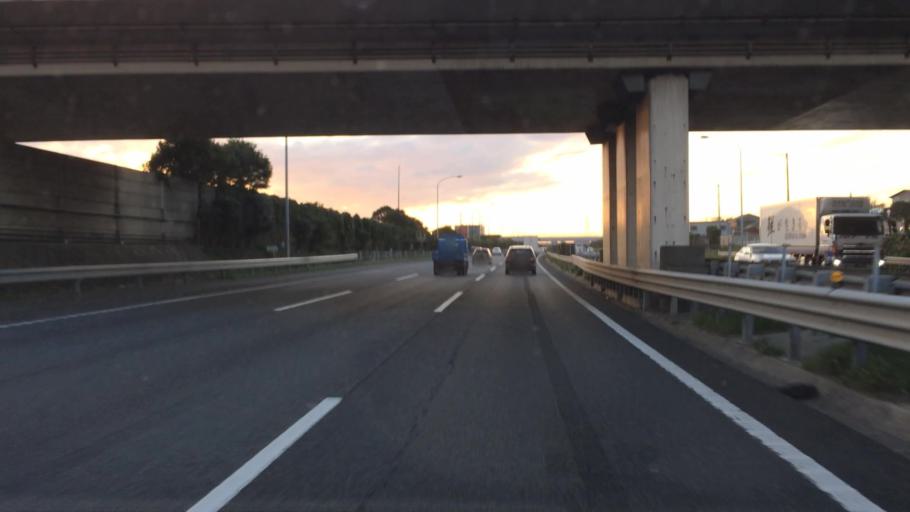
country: JP
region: Chiba
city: Yotsukaido
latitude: 35.6823
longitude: 140.1608
